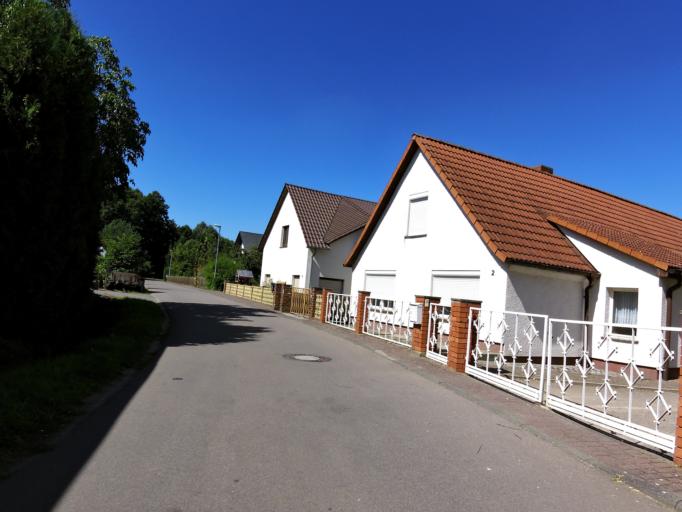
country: DE
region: Saxony
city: Torgau
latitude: 51.5121
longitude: 13.0280
